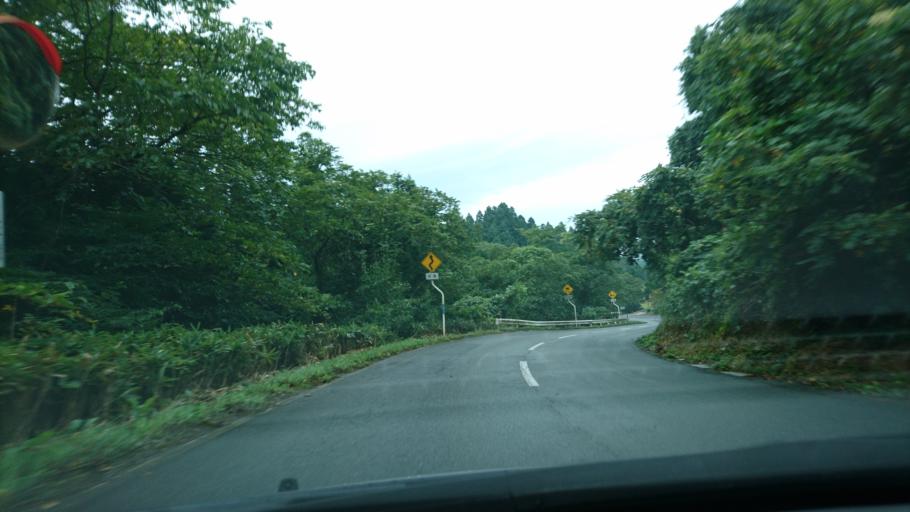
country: JP
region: Iwate
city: Mizusawa
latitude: 39.0393
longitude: 141.1903
